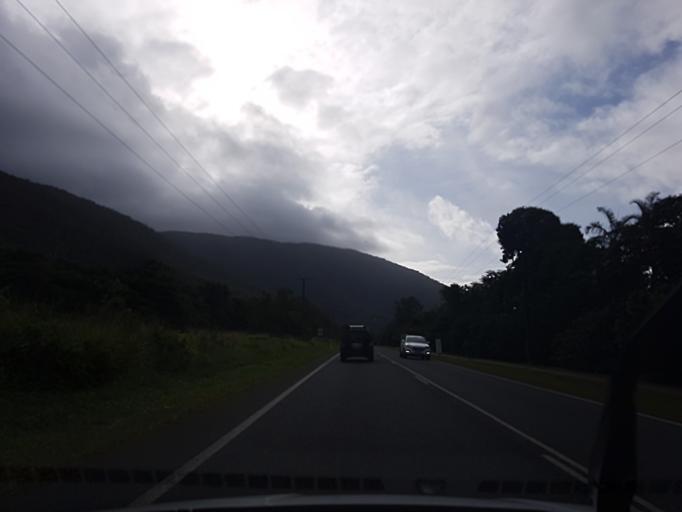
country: AU
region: Queensland
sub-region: Cairns
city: Palm Cove
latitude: -16.7634
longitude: 145.6669
